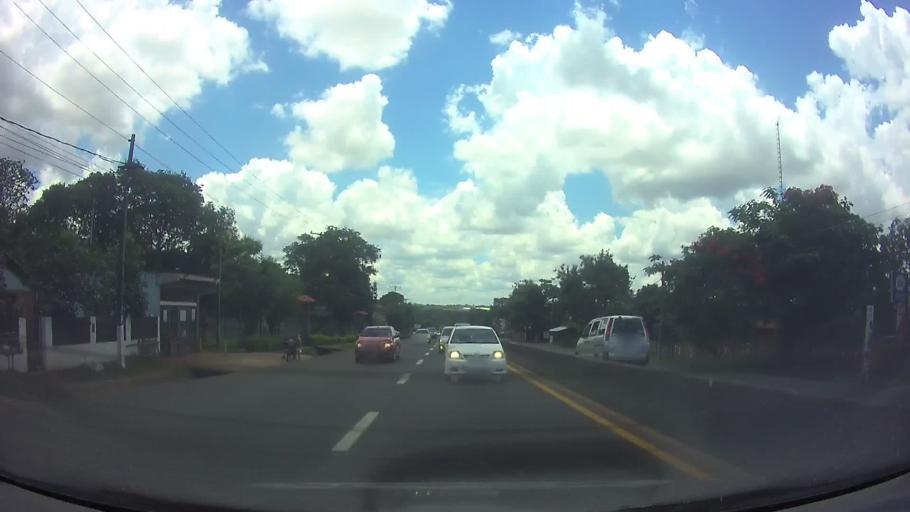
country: PY
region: Central
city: Capiata
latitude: -25.3781
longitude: -57.3955
